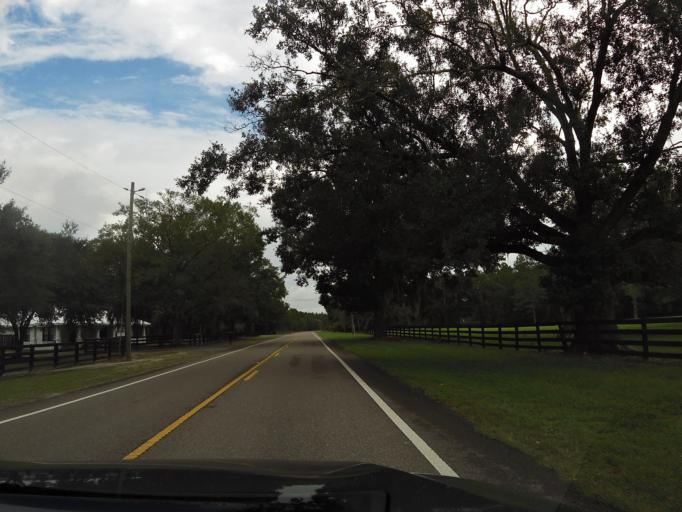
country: US
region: Florida
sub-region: Duval County
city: Baldwin
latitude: 30.3632
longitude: -81.9199
